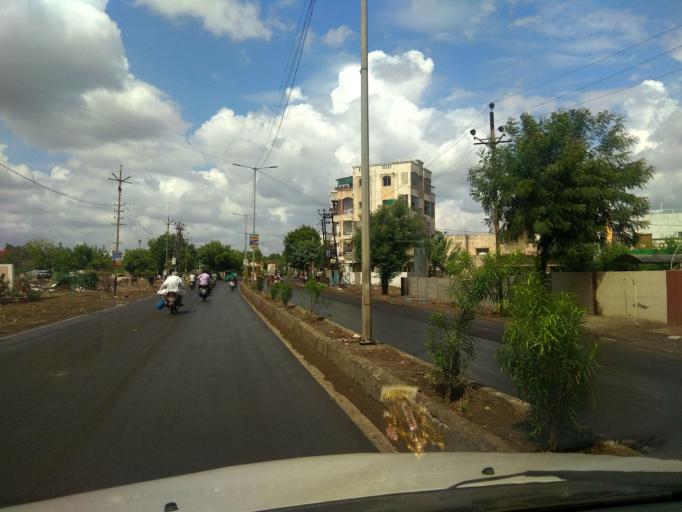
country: IN
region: Gujarat
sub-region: Bhavnagar
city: Bhavnagar
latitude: 21.7462
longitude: 72.1558
